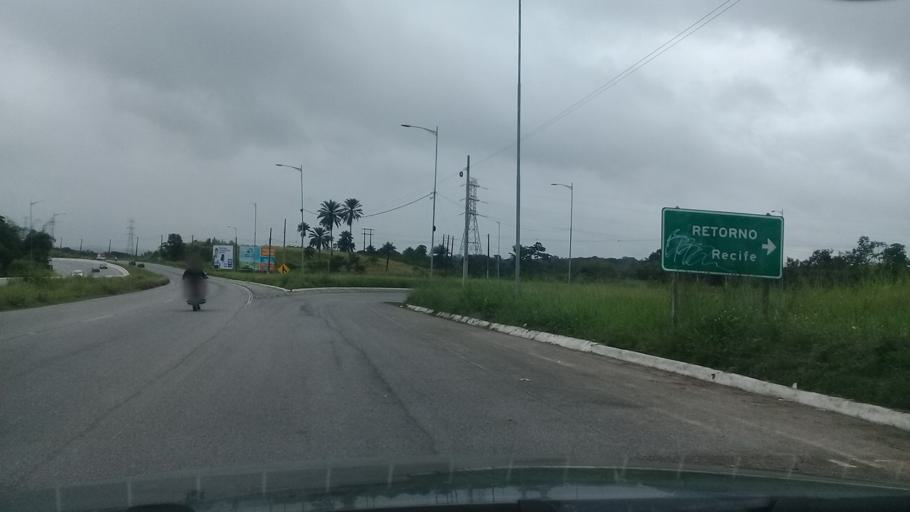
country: BR
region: Pernambuco
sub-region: Jaboatao Dos Guararapes
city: Jaboatao dos Guararapes
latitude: -8.0641
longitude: -34.9900
